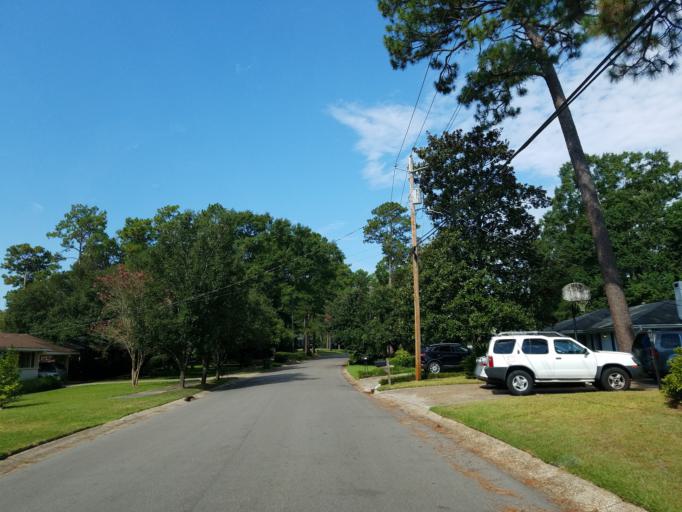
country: US
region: Mississippi
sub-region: Lamar County
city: West Hattiesburg
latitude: 31.3169
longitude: -89.3386
